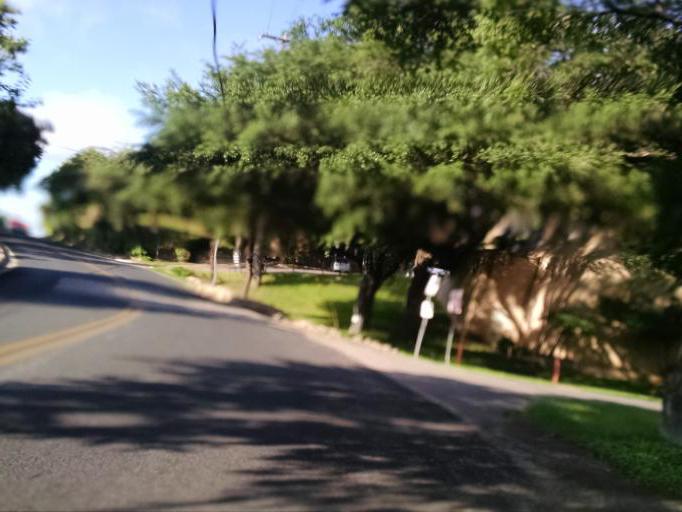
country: US
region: Texas
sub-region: Travis County
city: Austin
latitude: 30.2927
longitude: -97.7365
